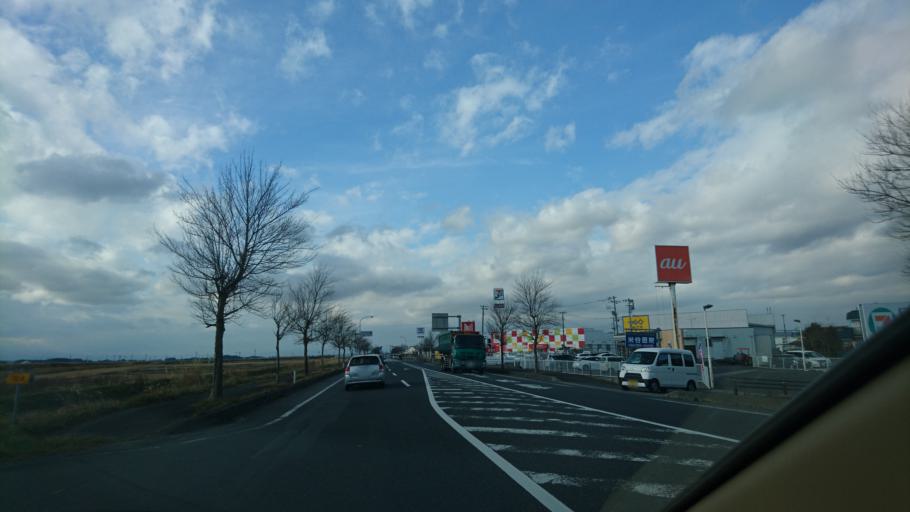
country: JP
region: Miyagi
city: Wakuya
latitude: 38.5310
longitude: 141.1296
